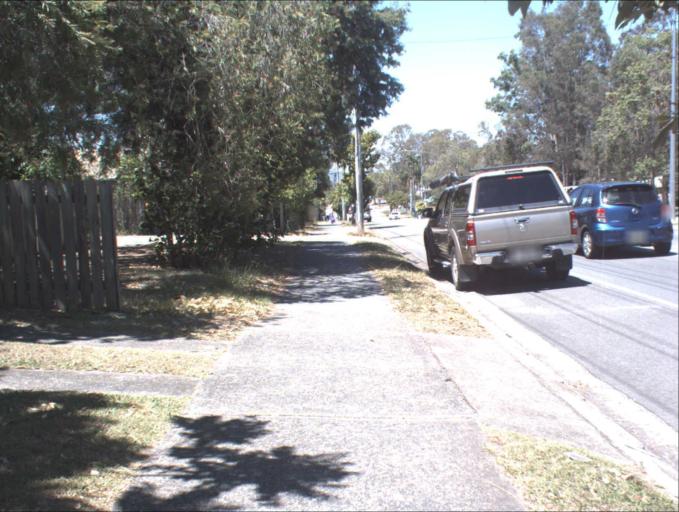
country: AU
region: Queensland
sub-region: Logan
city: Beenleigh
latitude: -27.7060
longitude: 153.2125
